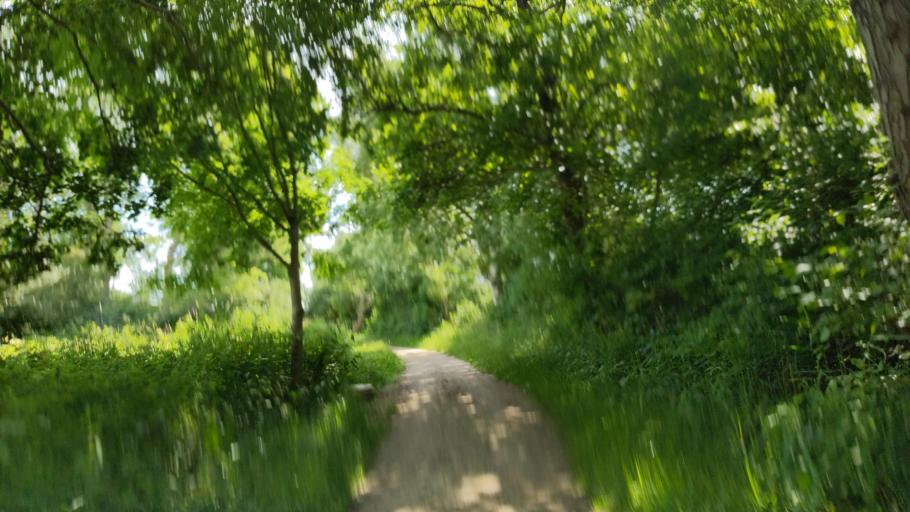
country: DE
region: Schleswig-Holstein
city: Eutin
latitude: 54.1382
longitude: 10.6352
